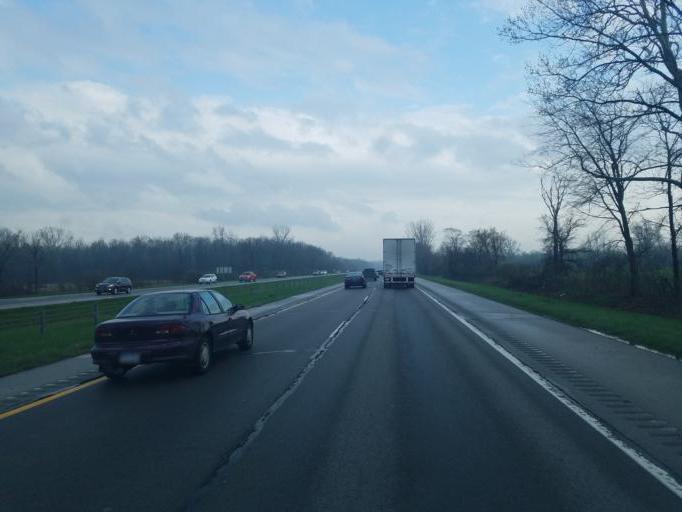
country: US
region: Michigan
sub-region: Washtenaw County
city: Milan
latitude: 42.0583
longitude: -83.6704
